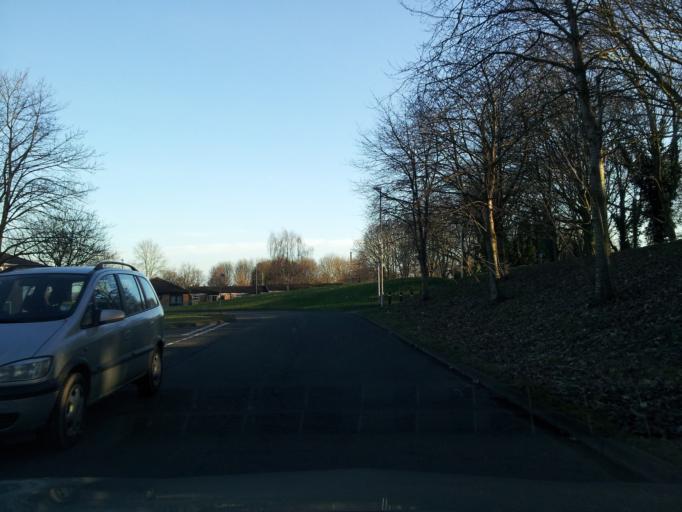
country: GB
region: England
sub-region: Northamptonshire
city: Northampton
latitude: 52.2543
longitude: -0.9375
